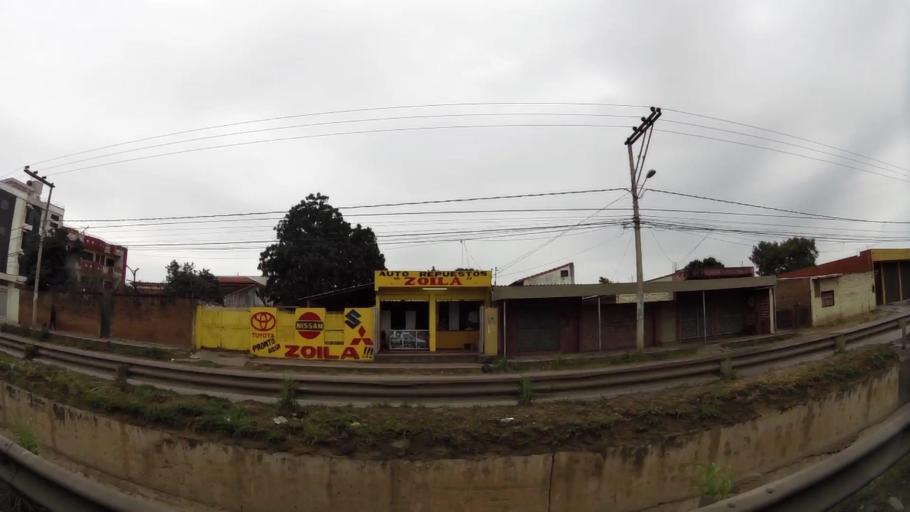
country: BO
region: Santa Cruz
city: Santa Cruz de la Sierra
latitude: -17.8264
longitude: -63.1688
